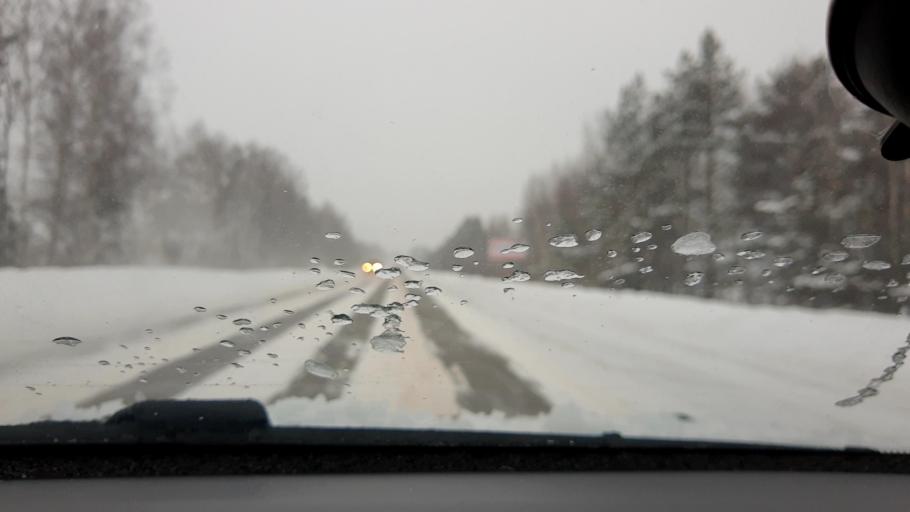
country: RU
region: Nizjnij Novgorod
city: Purekh
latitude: 56.6449
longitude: 43.0955
